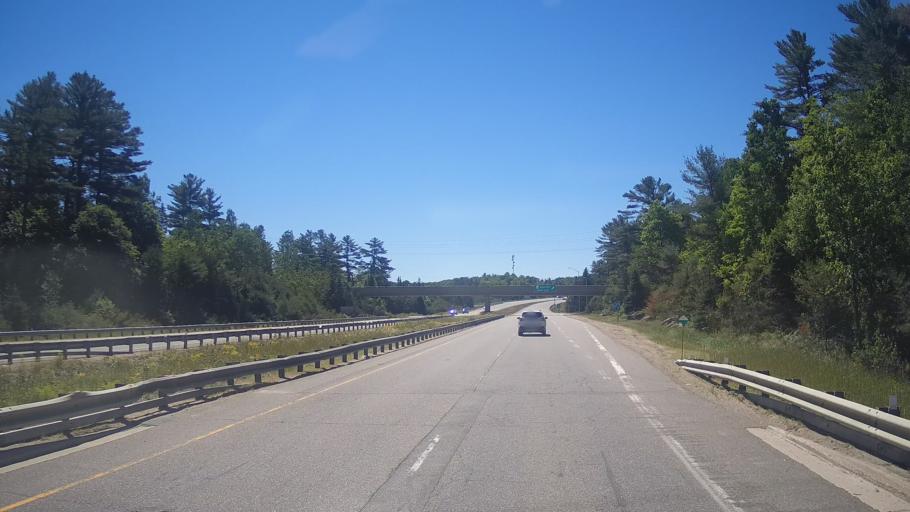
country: CA
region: Ontario
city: Bracebridge
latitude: 45.0882
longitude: -79.2997
